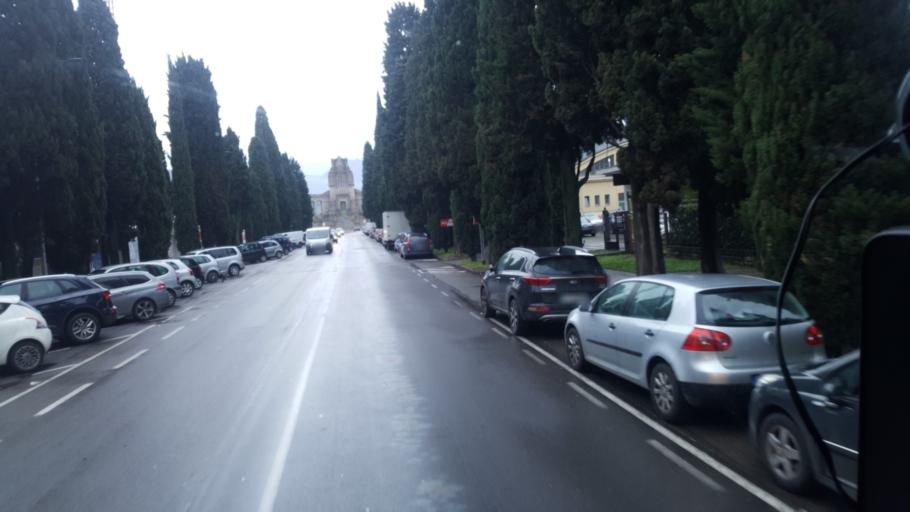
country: IT
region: Lombardy
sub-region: Provincia di Bergamo
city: Orio al Serio
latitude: 45.6960
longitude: 9.6894
